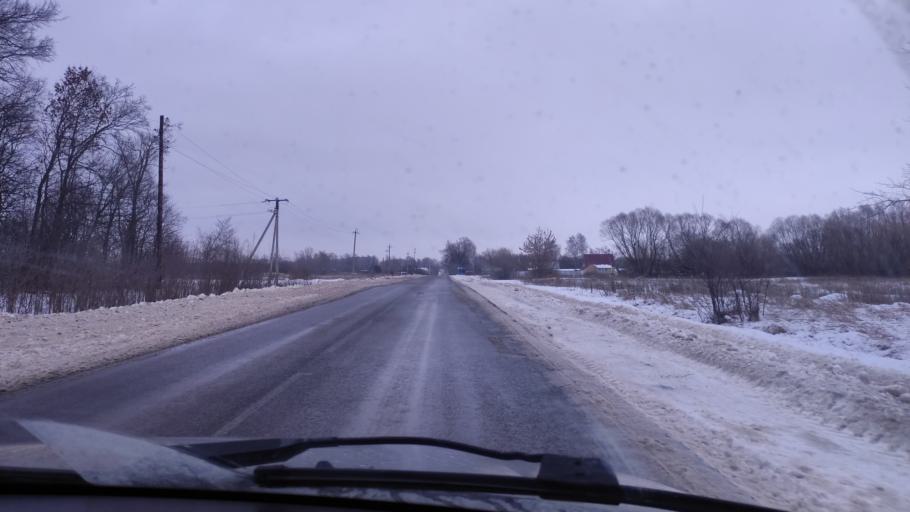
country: RU
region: Tambov
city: Pervomayskiy
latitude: 53.3018
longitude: 40.3668
